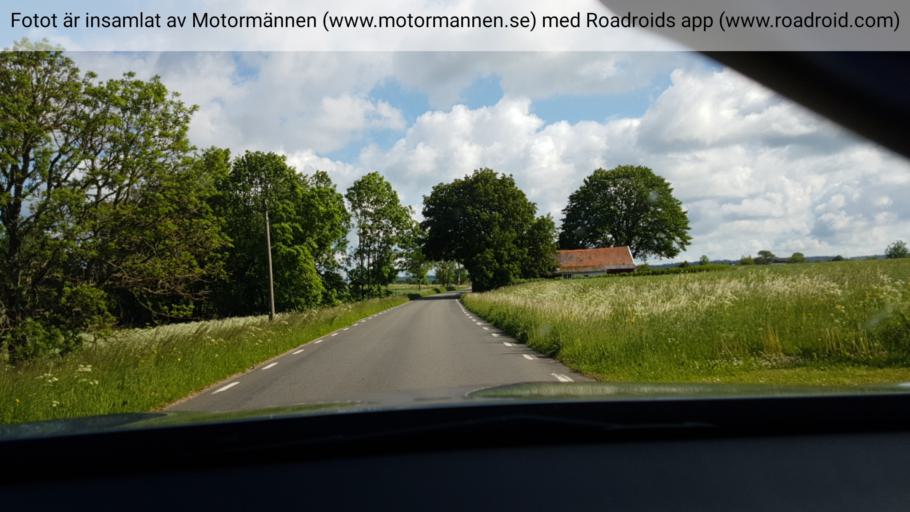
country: SE
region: Vaestra Goetaland
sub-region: Falkopings Kommun
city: Akarp
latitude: 58.3078
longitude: 13.6092
